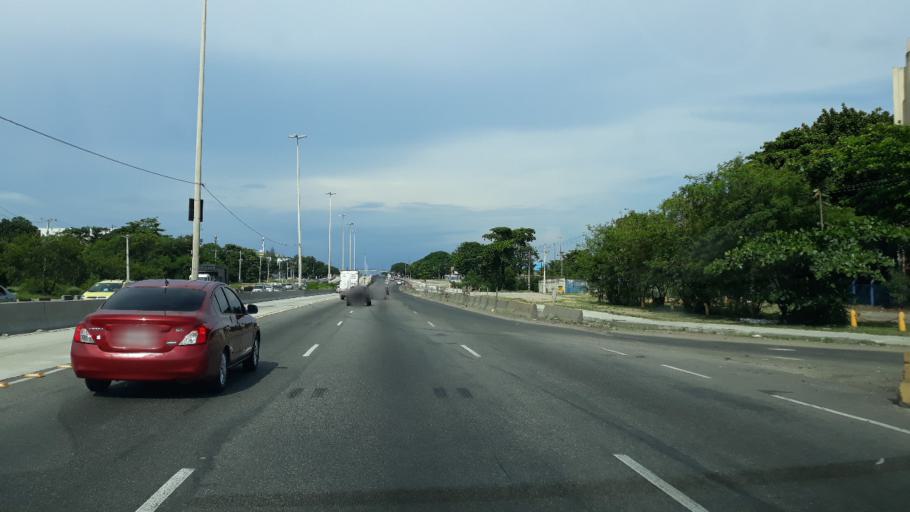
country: BR
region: Rio de Janeiro
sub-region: Sao Joao De Meriti
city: Sao Joao de Meriti
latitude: -22.8334
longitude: -43.3571
